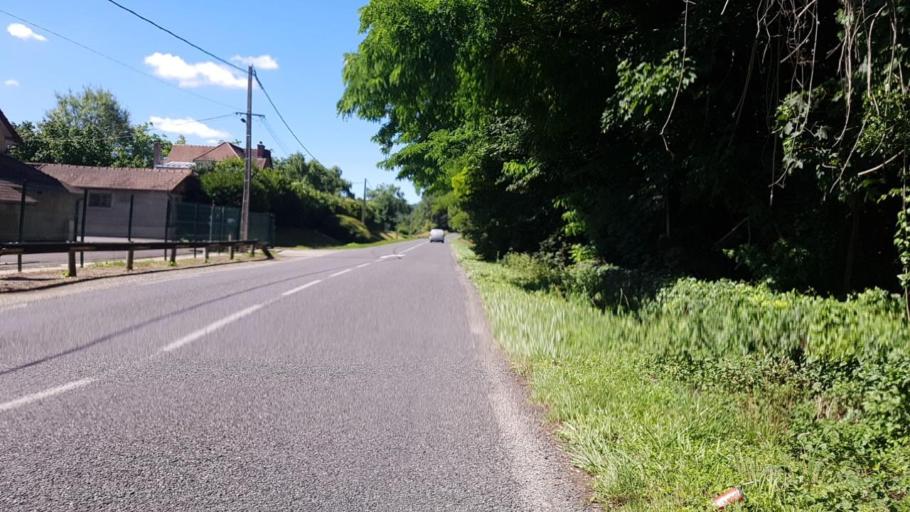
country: FR
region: Ile-de-France
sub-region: Departement de Seine-et-Marne
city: Saacy-sur-Marne
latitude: 48.9686
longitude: 3.2060
